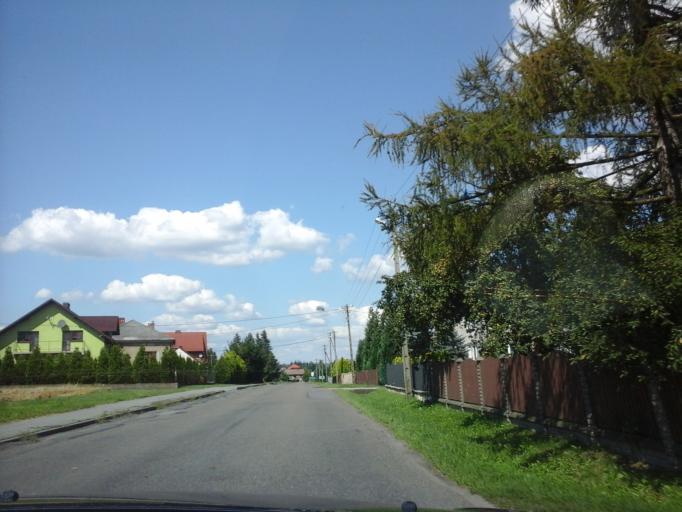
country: PL
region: Lesser Poland Voivodeship
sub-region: Powiat wadowicki
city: Spytkowice
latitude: 49.9902
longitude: 19.5012
